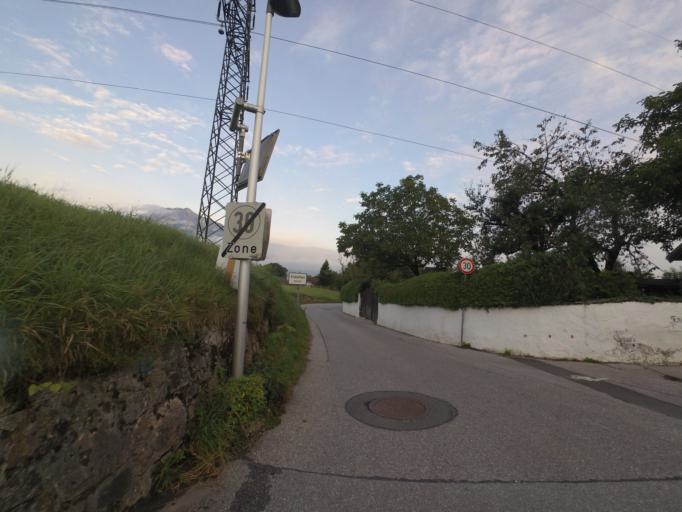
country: AT
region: Salzburg
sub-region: Politischer Bezirk Salzburg-Umgebung
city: Elsbethen
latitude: 47.7464
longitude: 13.0880
